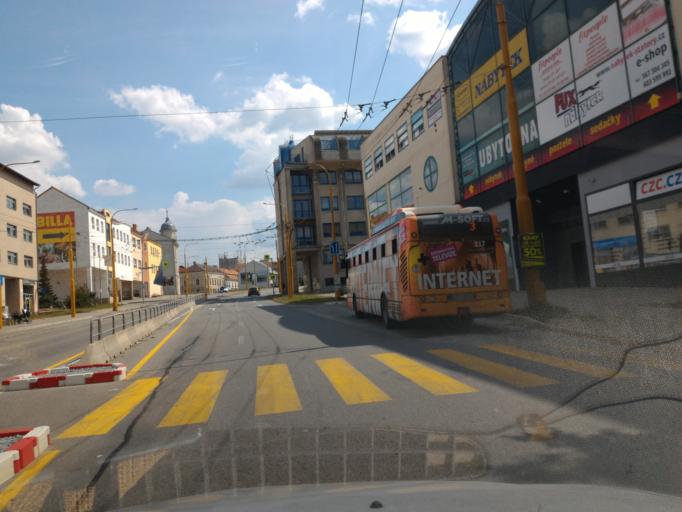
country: CZ
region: Vysocina
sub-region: Okres Jihlava
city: Jihlava
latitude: 49.4012
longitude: 15.5880
